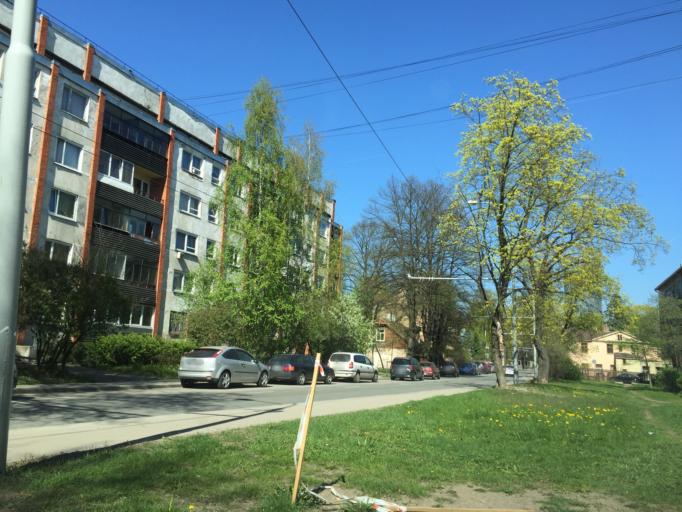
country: LV
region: Riga
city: Riga
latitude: 56.9430
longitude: 24.0717
